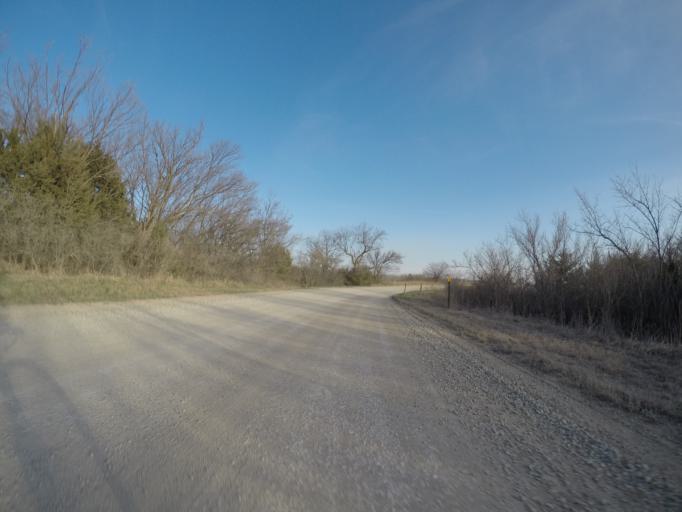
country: US
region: Kansas
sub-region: Riley County
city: Ogden
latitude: 39.2384
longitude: -96.6954
